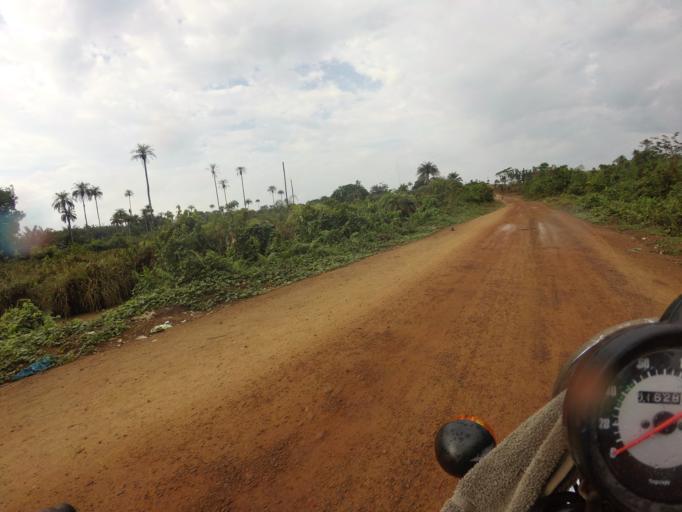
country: SL
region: Southern Province
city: Zimmi
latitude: 7.2197
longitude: -11.1774
